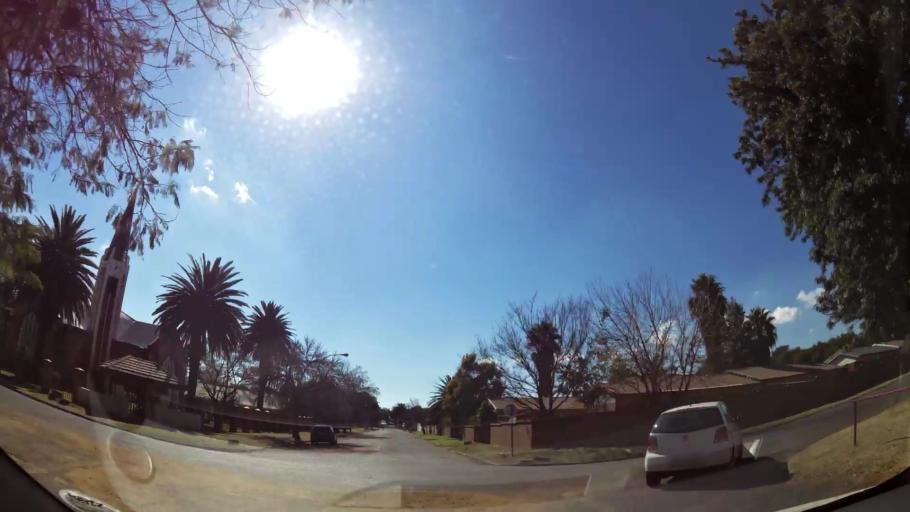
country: ZA
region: Mpumalanga
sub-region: Nkangala District Municipality
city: Witbank
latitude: -25.8699
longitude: 29.2160
